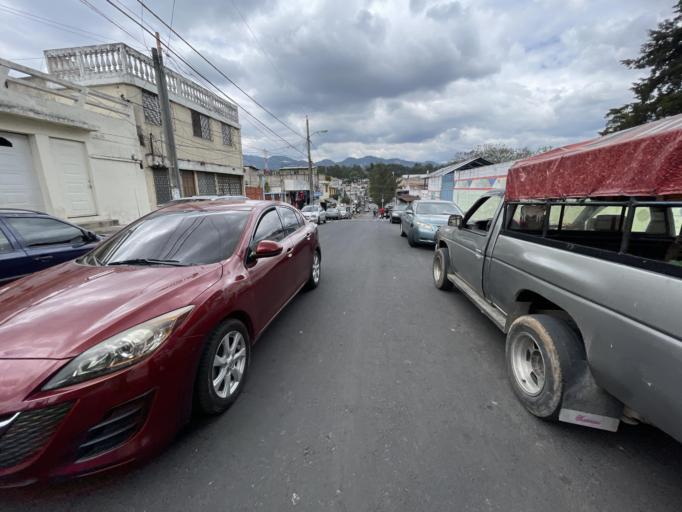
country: GT
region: Guatemala
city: Mixco
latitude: 14.6611
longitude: -90.5847
